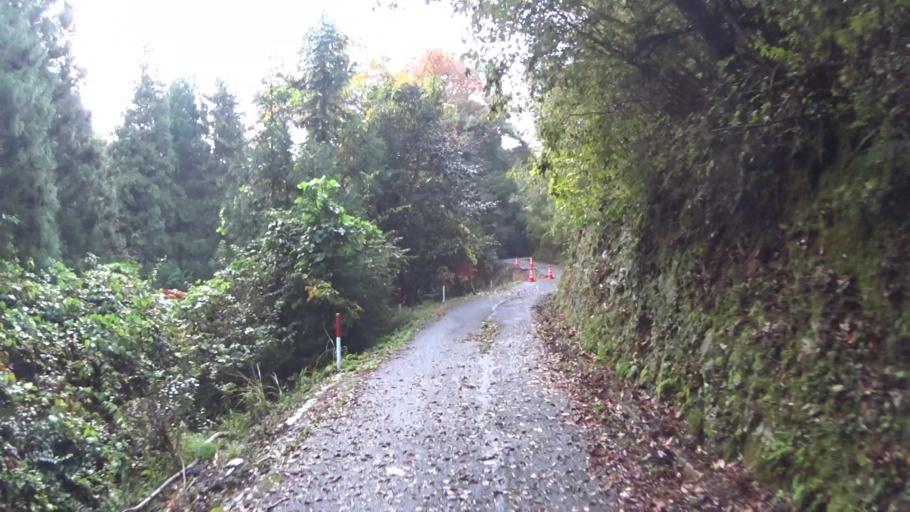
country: JP
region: Kyoto
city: Ayabe
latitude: 35.2699
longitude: 135.2254
